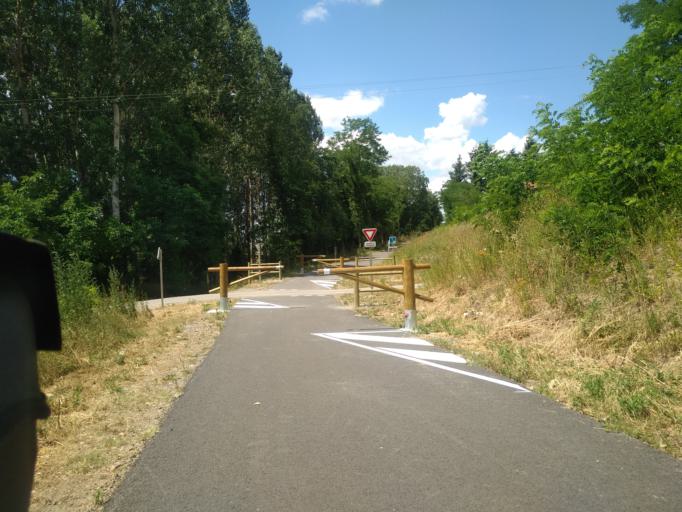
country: FR
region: Rhone-Alpes
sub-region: Departement de la Loire
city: Briennon
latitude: 46.1867
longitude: 4.0868
